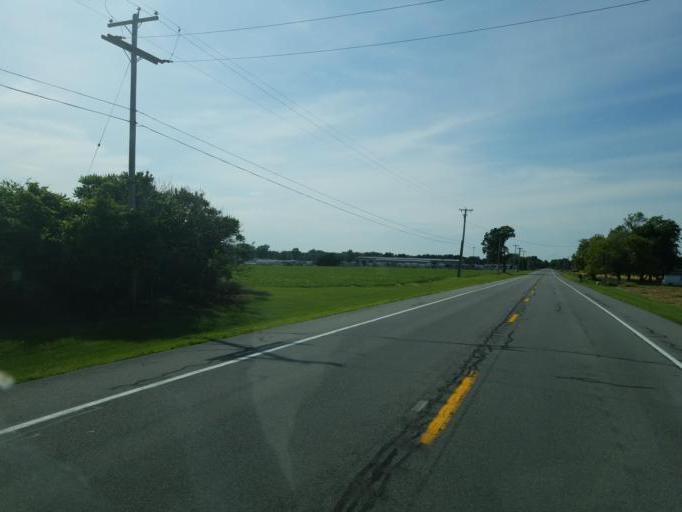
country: US
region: New York
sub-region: Livingston County
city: Caledonia
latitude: 42.9613
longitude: -77.8394
